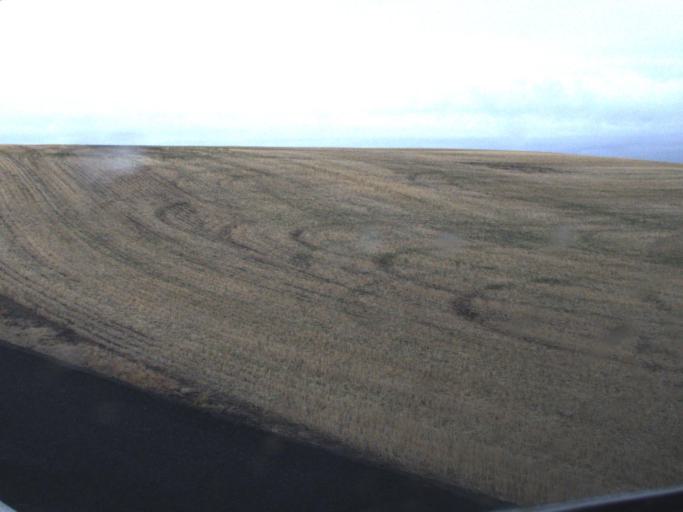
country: US
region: Washington
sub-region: Whitman County
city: Pullman
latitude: 46.5698
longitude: -117.1397
